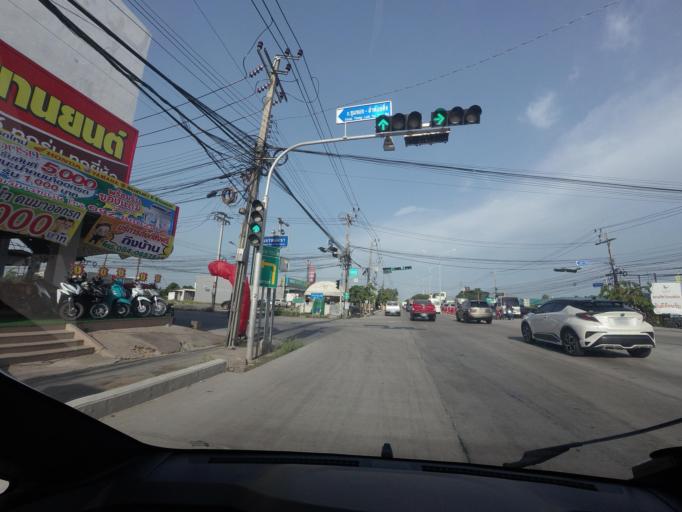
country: TH
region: Samut Prakan
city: Ban Khlong Bang Sao Thong
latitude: 13.6980
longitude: 100.8511
